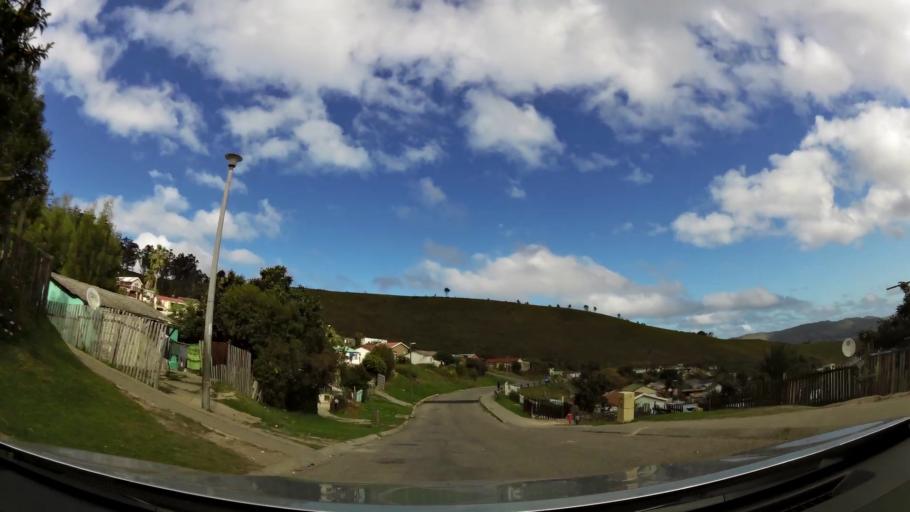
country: ZA
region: Western Cape
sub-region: Eden District Municipality
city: Knysna
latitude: -34.0532
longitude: 23.1053
